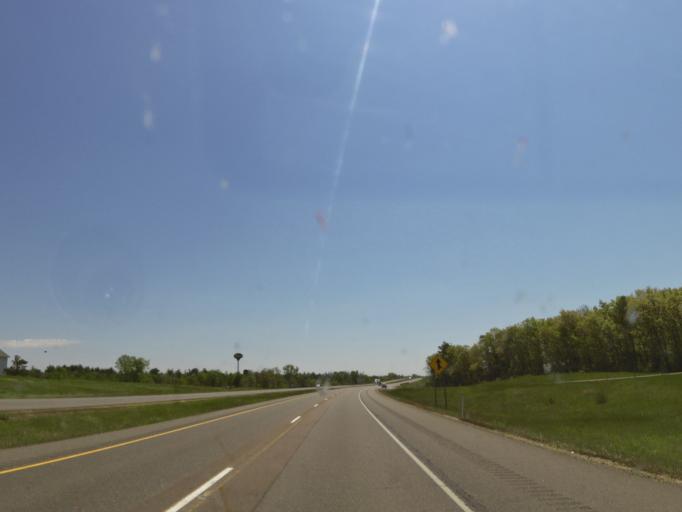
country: US
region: Wisconsin
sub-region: Monroe County
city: Tomah
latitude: 44.0182
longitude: -90.4968
